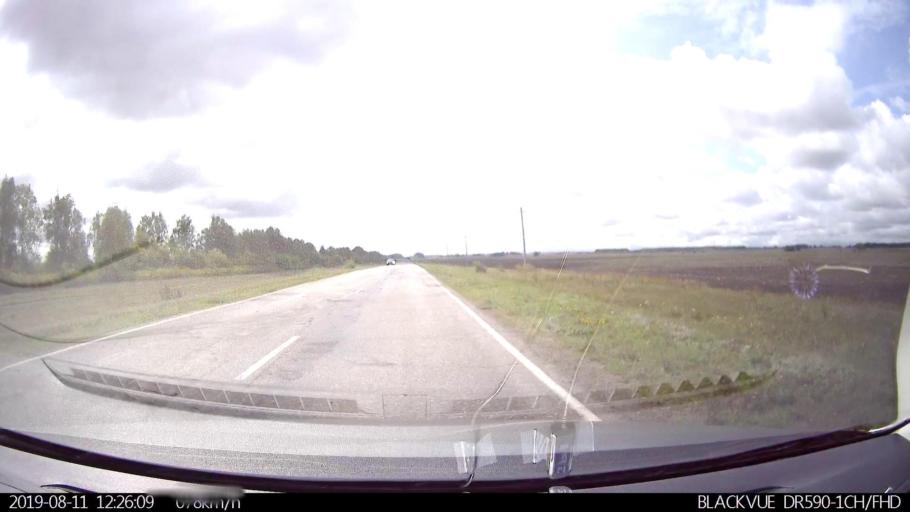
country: RU
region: Ulyanovsk
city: Ignatovka
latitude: 53.8667
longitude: 47.9327
